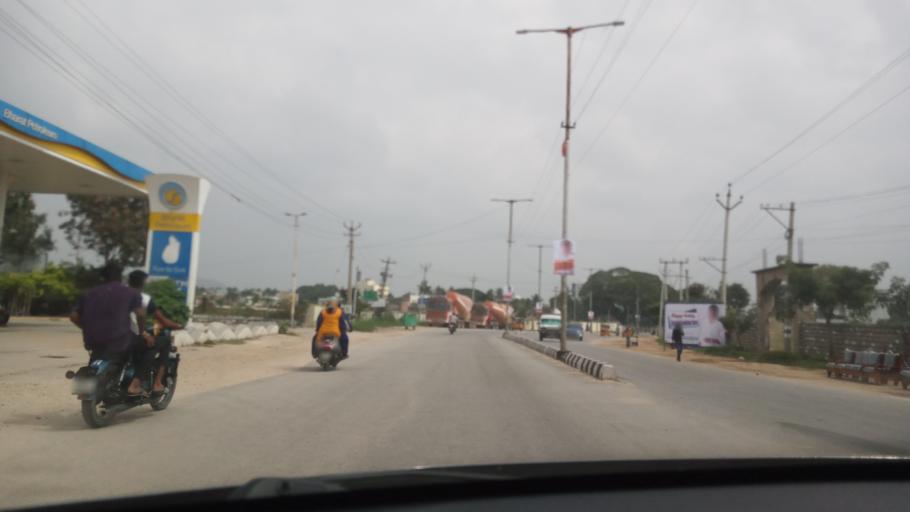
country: IN
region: Andhra Pradesh
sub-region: Chittoor
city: Madanapalle
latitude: 13.5555
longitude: 78.4928
